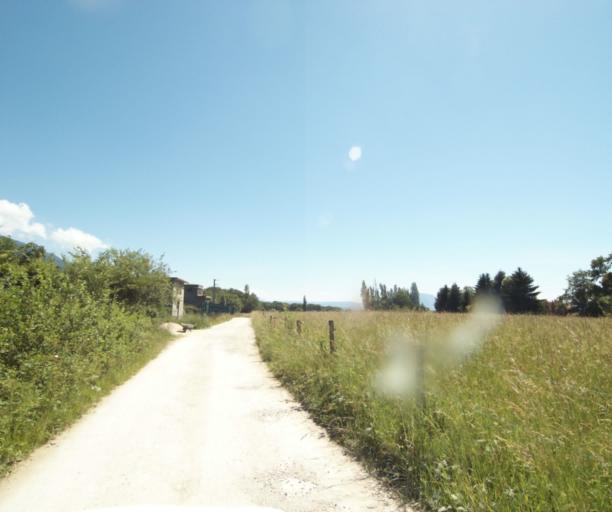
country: FR
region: Rhone-Alpes
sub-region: Departement de la Haute-Savoie
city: Loisin
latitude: 46.2788
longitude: 6.3261
